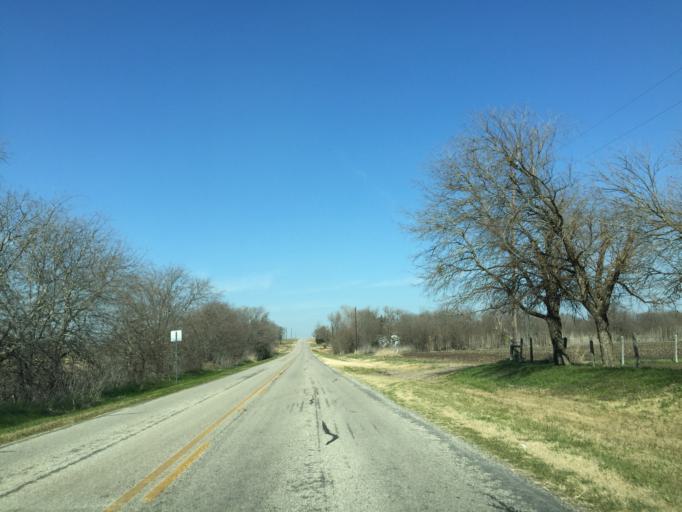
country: US
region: Texas
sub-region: Williamson County
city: Serenada
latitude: 30.6924
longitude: -97.5861
